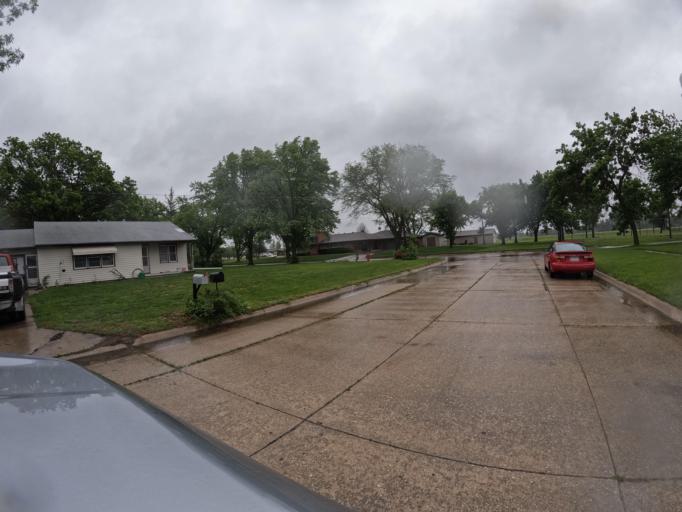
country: US
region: Nebraska
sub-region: Saline County
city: Wilber
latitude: 40.3938
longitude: -96.9252
